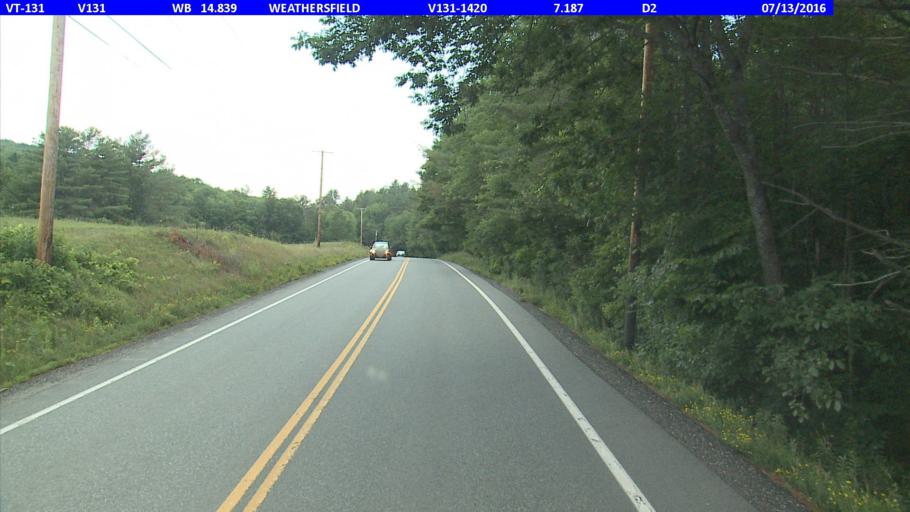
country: US
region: Vermont
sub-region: Windsor County
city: Windsor
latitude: 43.4052
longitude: -72.4324
